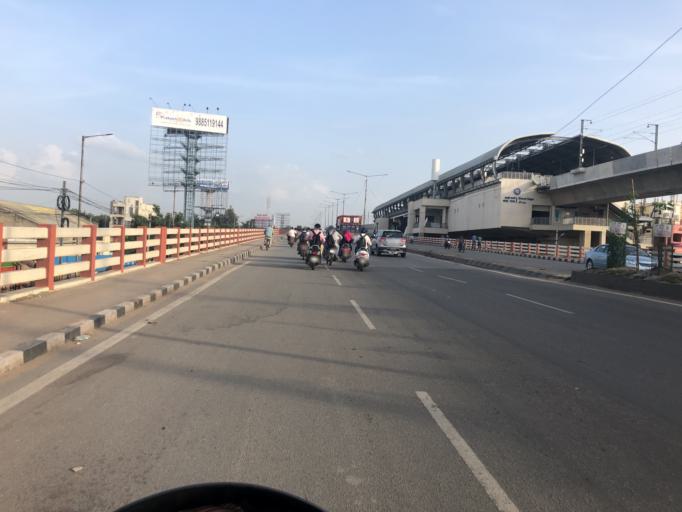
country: IN
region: Telangana
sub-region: Rangareddi
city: Kukatpalli
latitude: 17.4655
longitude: 78.4298
